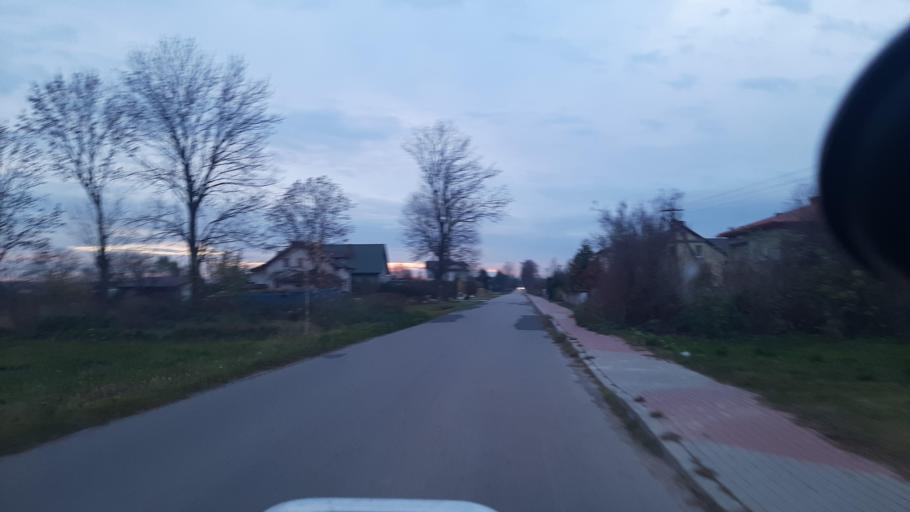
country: PL
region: Lublin Voivodeship
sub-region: Powiat lubelski
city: Garbow
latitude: 51.3652
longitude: 22.3838
